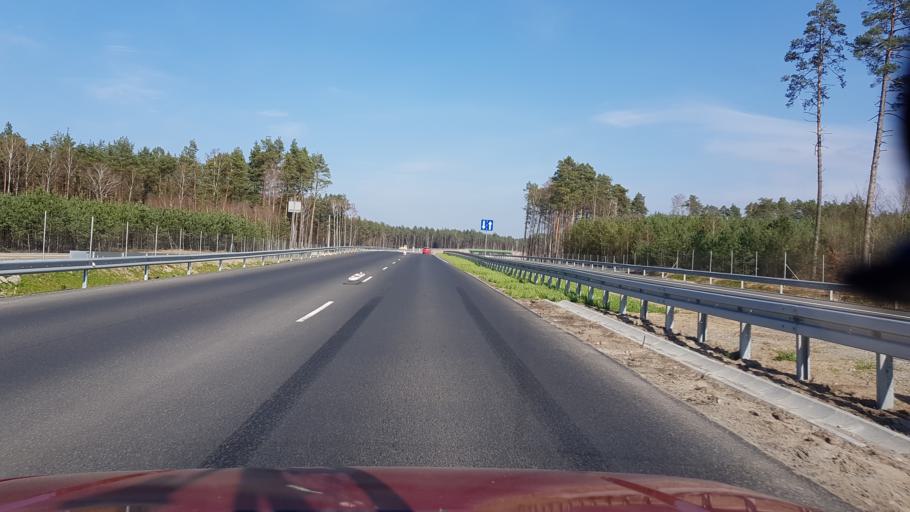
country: PL
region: West Pomeranian Voivodeship
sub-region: Powiat goleniowski
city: Mosty
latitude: 53.6084
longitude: 14.8990
